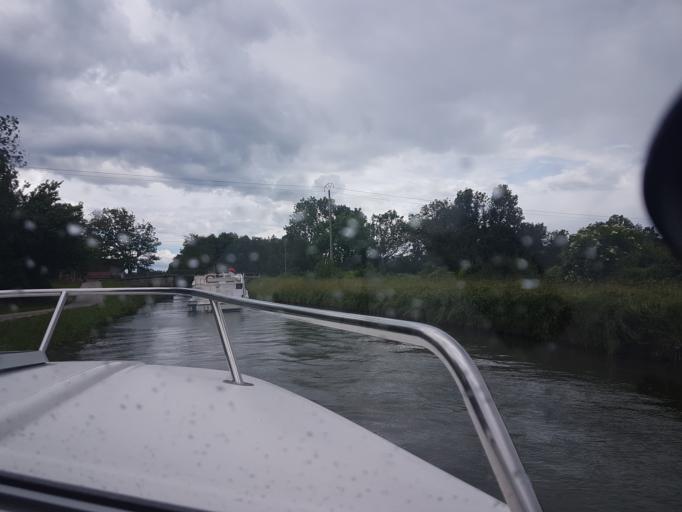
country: FR
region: Bourgogne
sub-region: Departement de la Nievre
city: Clamecy
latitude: 47.5510
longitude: 3.6310
